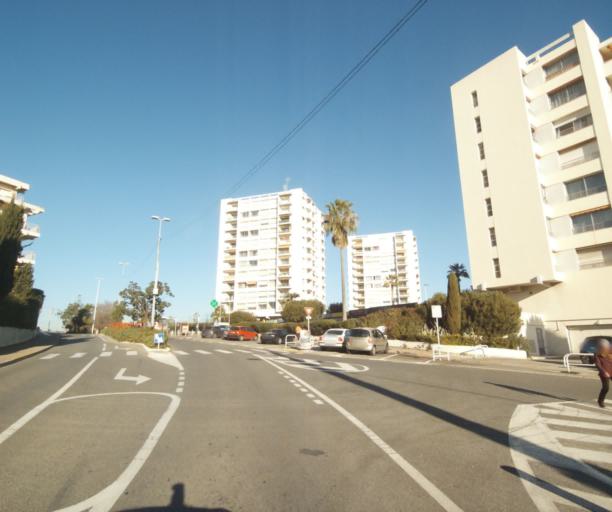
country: FR
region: Provence-Alpes-Cote d'Azur
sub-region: Departement des Alpes-Maritimes
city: Antibes
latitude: 43.5831
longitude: 7.1091
